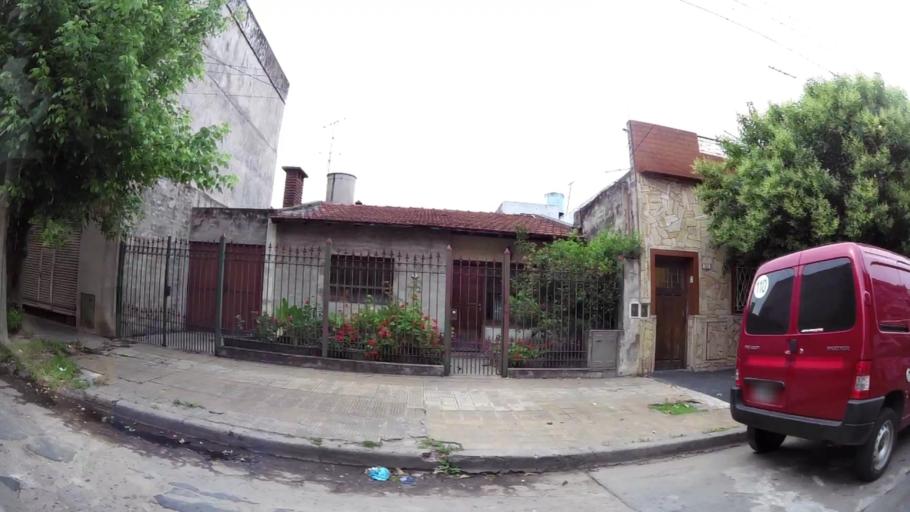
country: AR
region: Buenos Aires
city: San Justo
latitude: -34.6856
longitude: -58.5171
